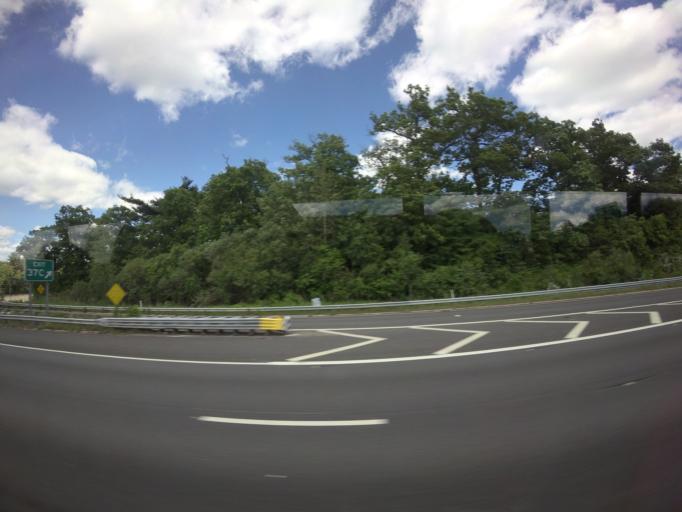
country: US
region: Massachusetts
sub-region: Middlesex County
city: Reading
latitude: 42.5175
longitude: -71.1310
